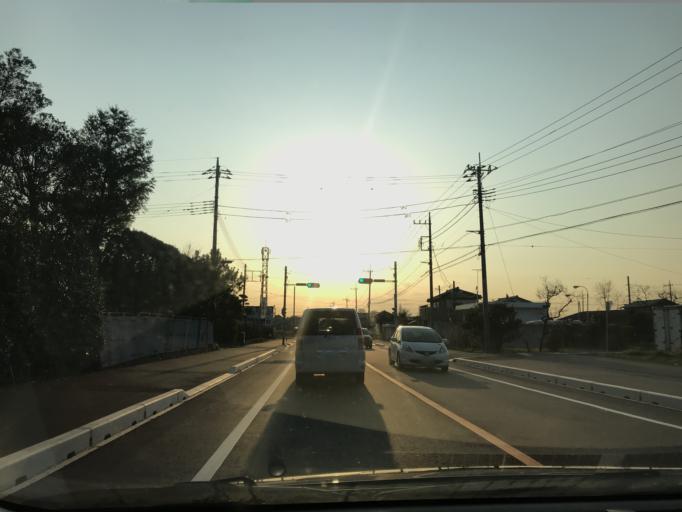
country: JP
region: Ibaraki
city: Mitsukaido
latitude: 35.9918
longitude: 140.0221
